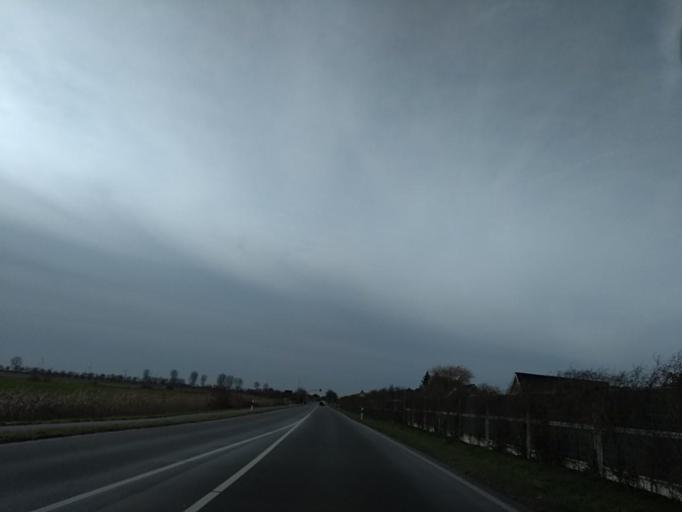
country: DE
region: Lower Saxony
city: Emden
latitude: 53.3615
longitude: 7.1380
